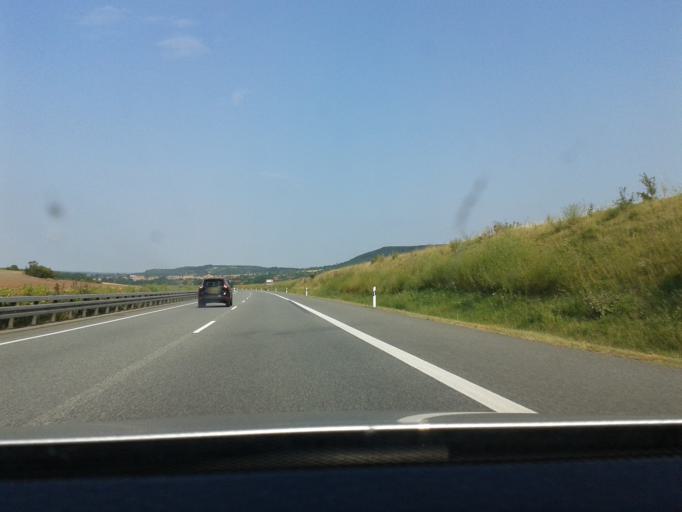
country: DE
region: Thuringia
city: Bleicherode
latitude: 51.4177
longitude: 10.5681
